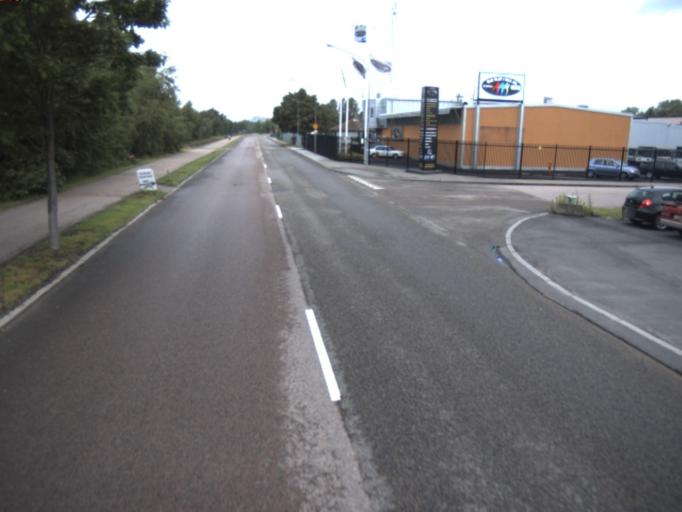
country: SE
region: Skane
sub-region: Helsingborg
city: Helsingborg
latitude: 56.0078
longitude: 12.7242
